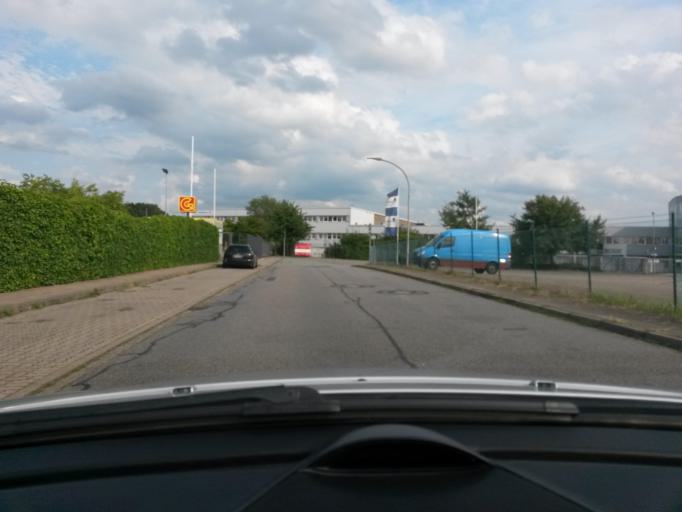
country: DE
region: Schleswig-Holstein
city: Barsbuettel
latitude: 53.5677
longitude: 10.1848
